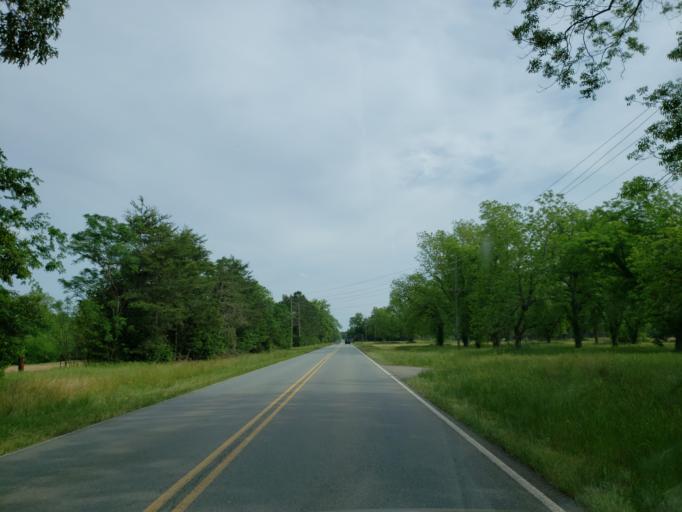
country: US
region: Georgia
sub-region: Dooly County
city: Vienna
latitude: 32.1807
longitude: -83.8935
